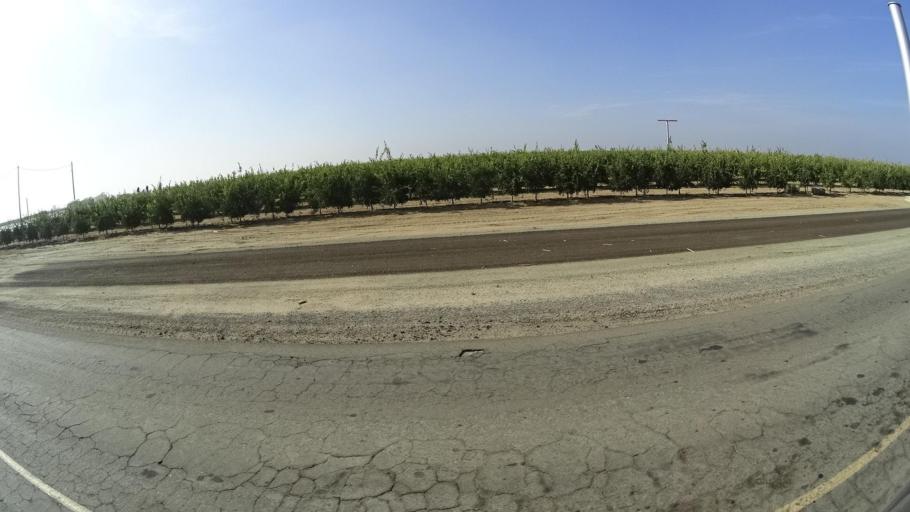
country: US
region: California
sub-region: Kern County
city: McFarland
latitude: 35.6244
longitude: -119.1688
